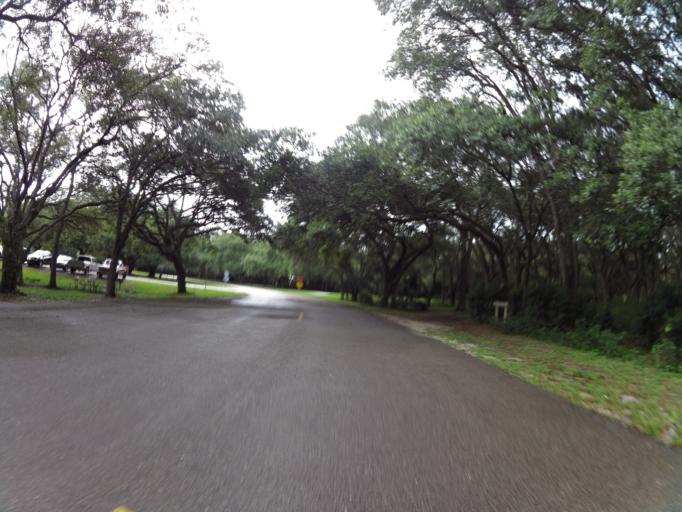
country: US
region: Florida
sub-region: Broward County
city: Cooper City
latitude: 26.0684
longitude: -80.2749
